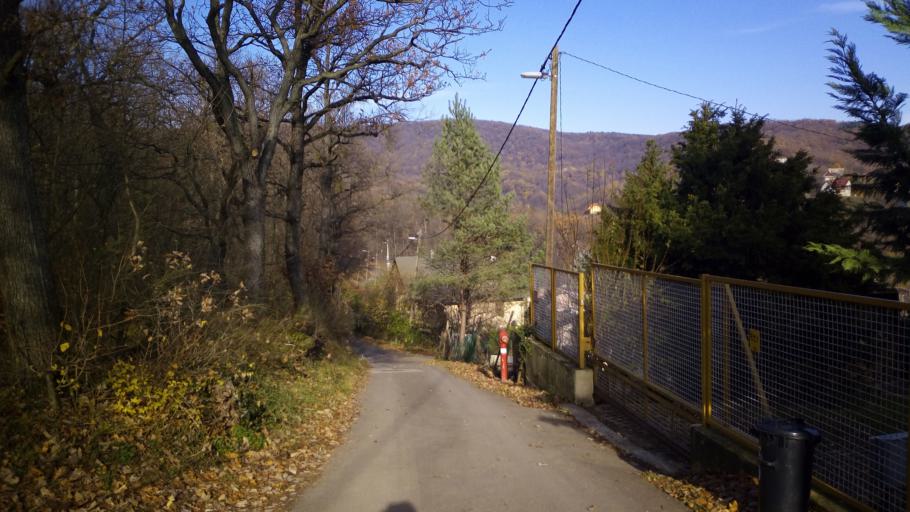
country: HU
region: Baranya
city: Pecs
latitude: 46.0949
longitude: 18.1815
